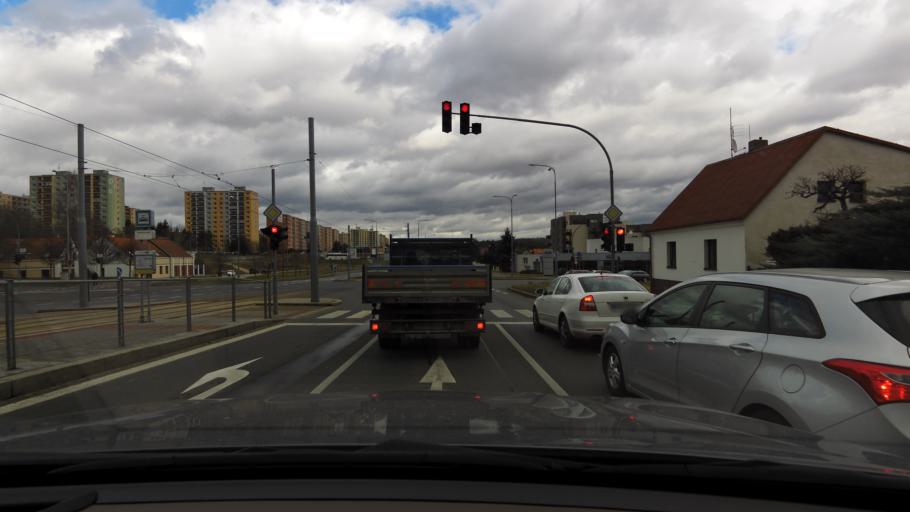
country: CZ
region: Plzensky
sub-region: Okres Plzen-Mesto
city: Pilsen
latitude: 49.7747
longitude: 13.3793
